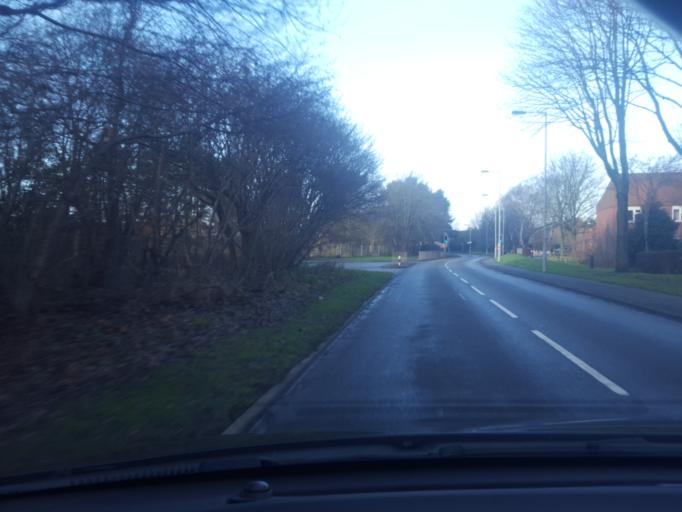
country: GB
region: England
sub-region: Staffordshire
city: Codsall
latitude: 52.6167
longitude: -2.1613
